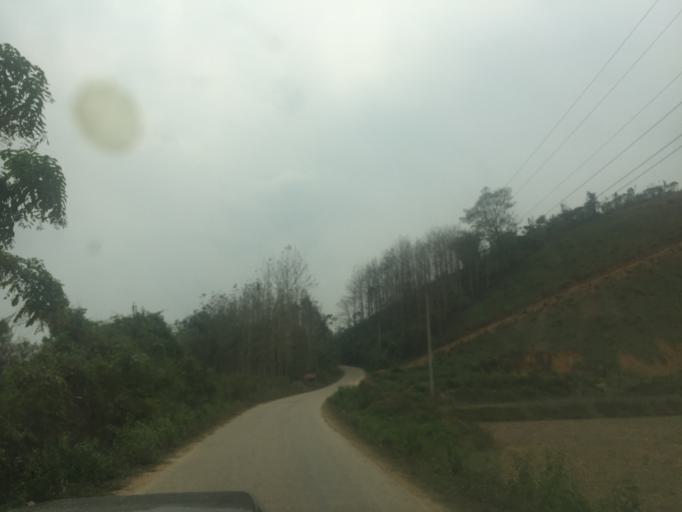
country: LA
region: Vientiane
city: Muang Sanakham
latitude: 18.3853
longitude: 101.5380
